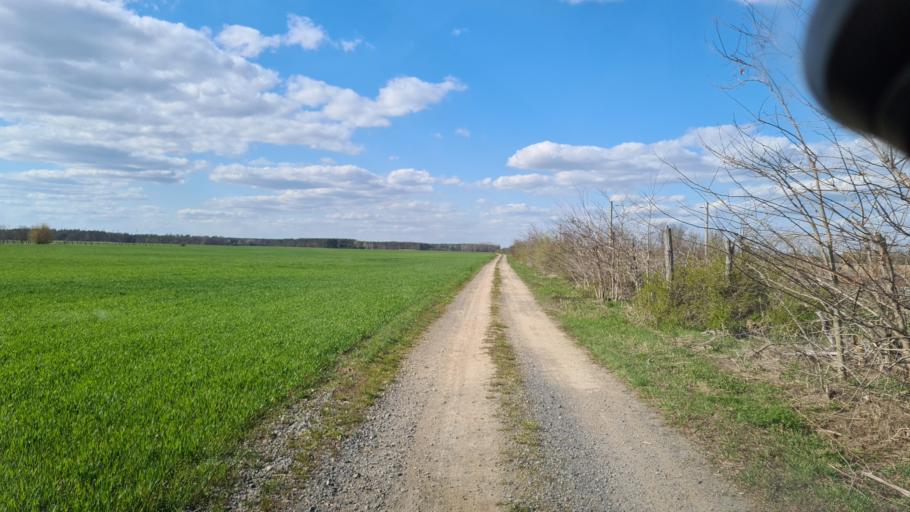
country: DE
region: Brandenburg
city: Falkenberg
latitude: 51.5109
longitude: 13.2763
